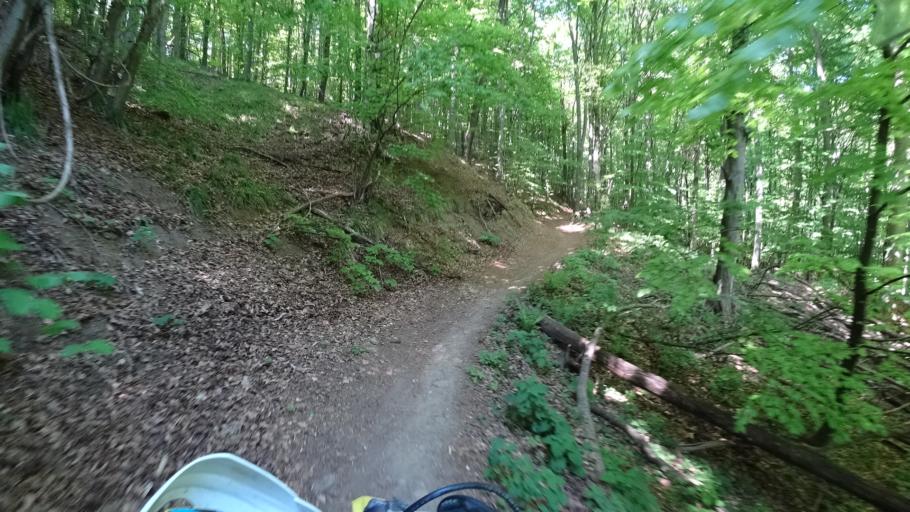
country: HR
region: Zagrebacka
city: Jablanovec
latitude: 45.8788
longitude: 15.8967
